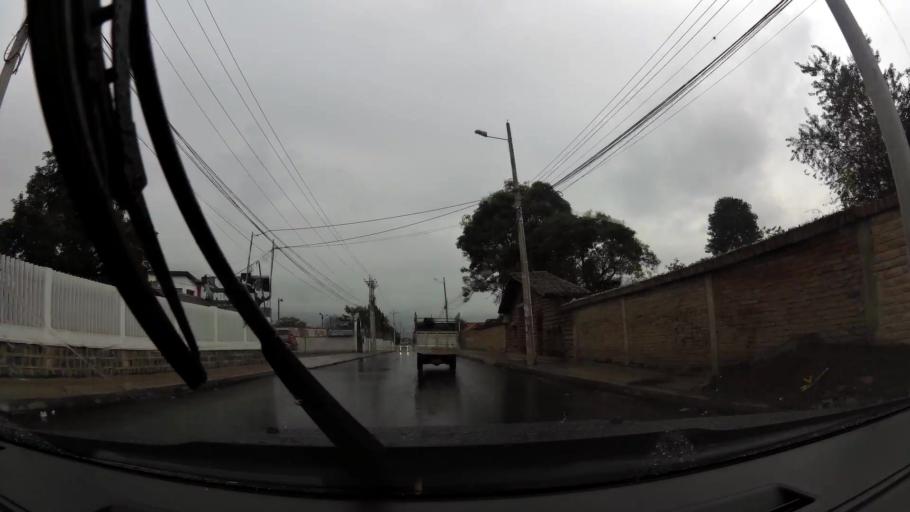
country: EC
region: Pichincha
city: Sangolqui
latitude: -0.3023
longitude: -78.4491
